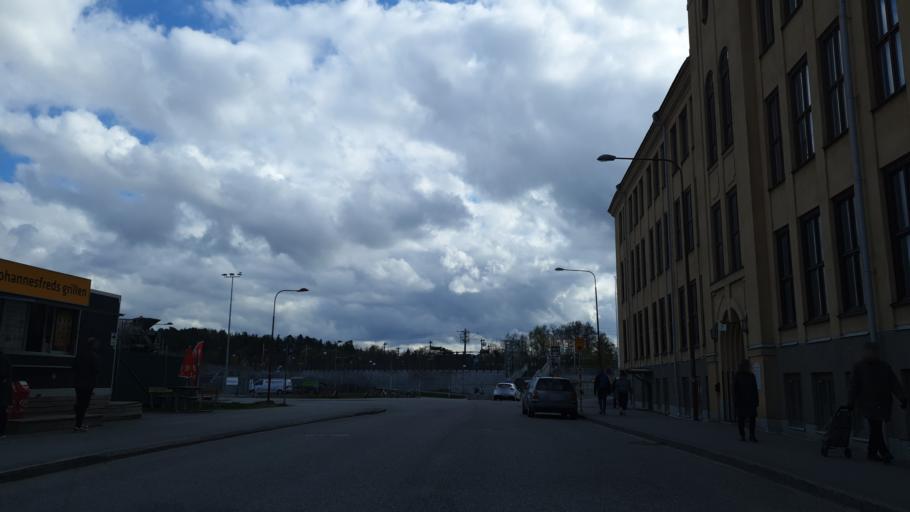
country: SE
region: Stockholm
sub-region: Sundbybergs Kommun
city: Sundbyberg
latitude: 59.3439
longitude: 17.9697
